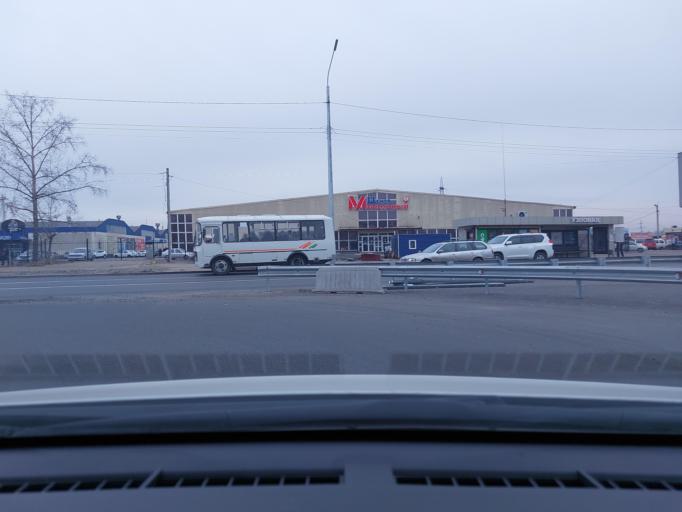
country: RU
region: Irkutsk
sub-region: Irkutskiy Rayon
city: Irkutsk
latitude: 52.3291
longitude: 104.2340
